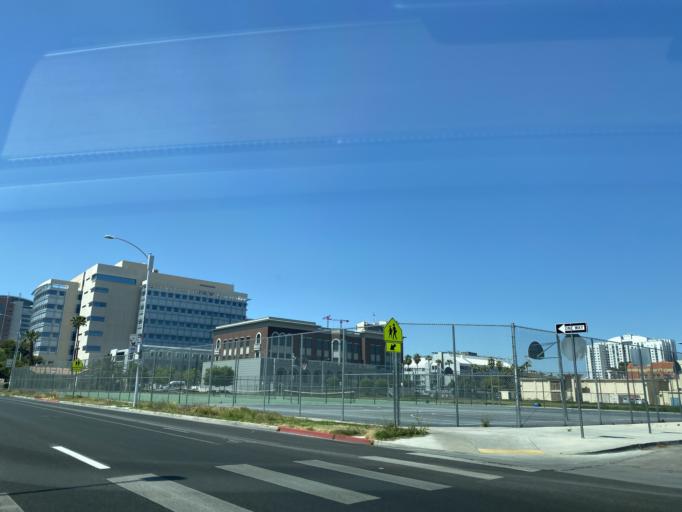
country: US
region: Nevada
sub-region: Clark County
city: Las Vegas
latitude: 36.1631
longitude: -115.1403
